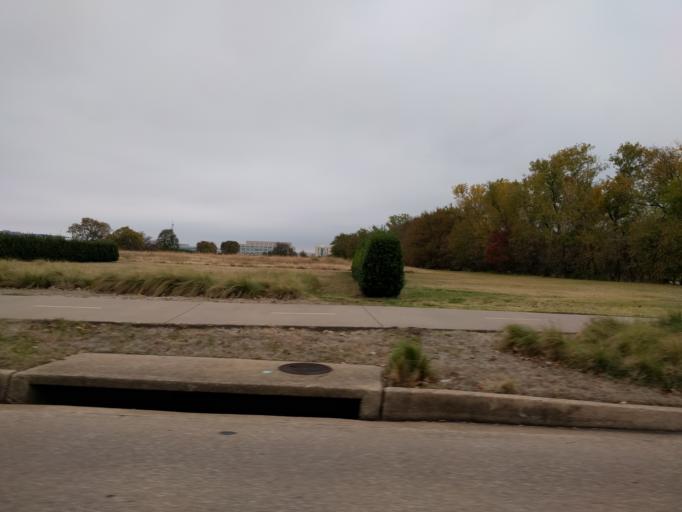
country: US
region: Texas
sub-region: Dallas County
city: Richardson
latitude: 32.9783
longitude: -96.7459
